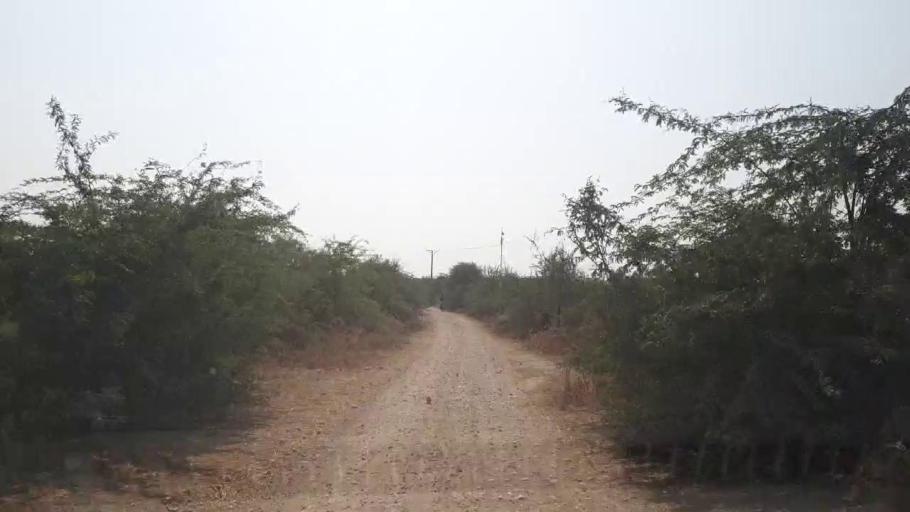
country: PK
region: Sindh
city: Kario
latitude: 24.9055
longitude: 68.5755
